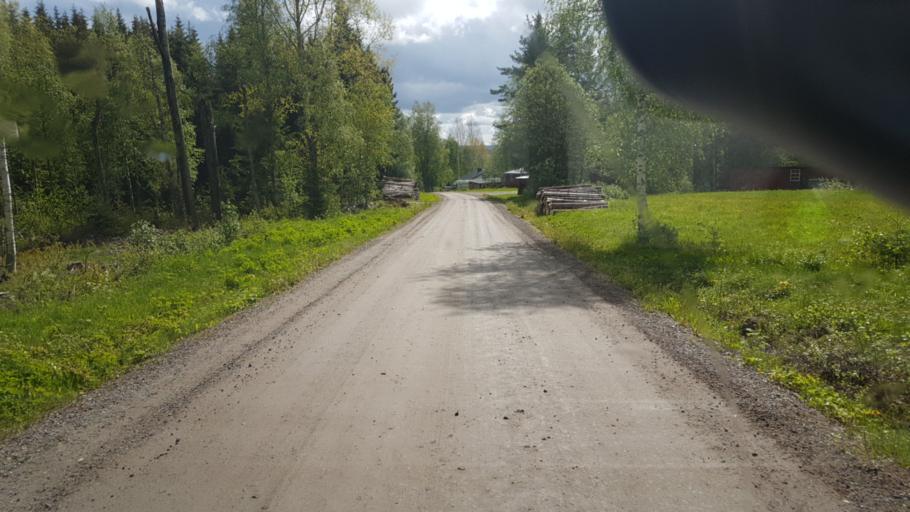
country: NO
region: Ostfold
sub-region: Romskog
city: Romskog
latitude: 59.7022
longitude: 12.0563
